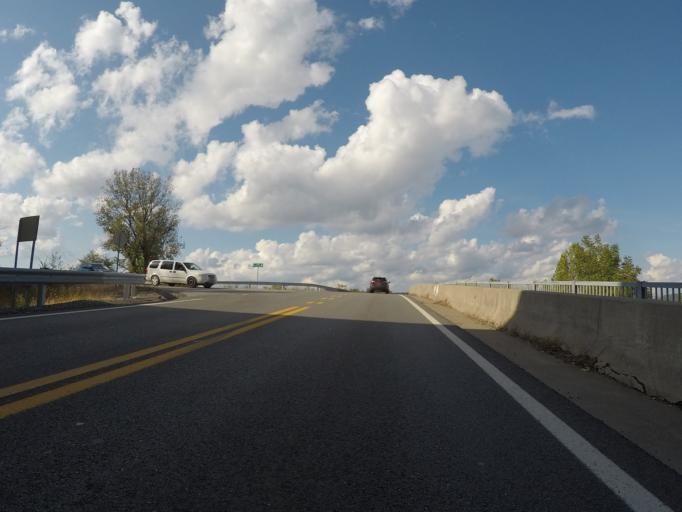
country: US
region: Ohio
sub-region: Lawrence County
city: Burlington
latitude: 38.3957
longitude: -82.5163
